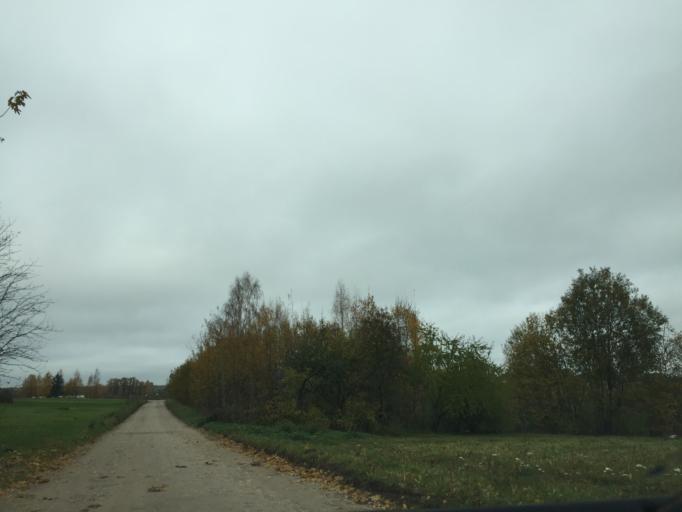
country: LV
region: Sigulda
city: Sigulda
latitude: 57.2432
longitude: 24.8281
